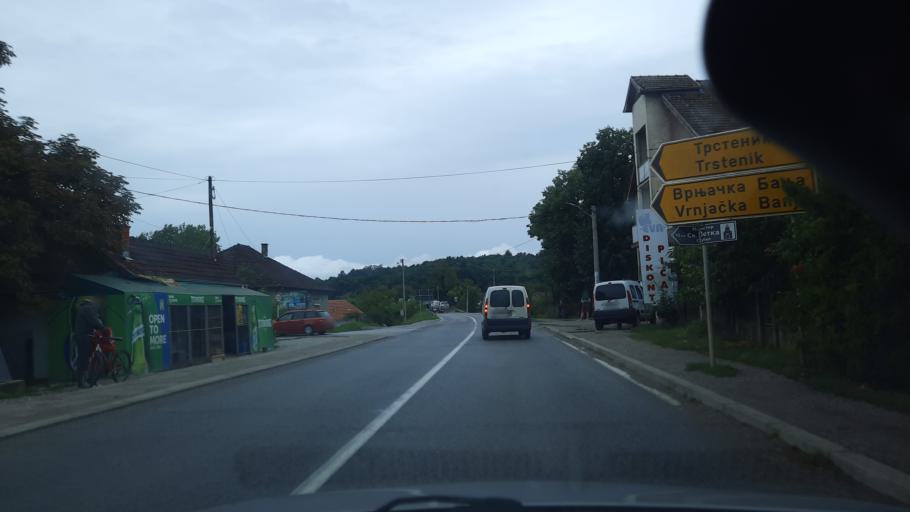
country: RS
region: Central Serbia
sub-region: Raski Okrug
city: Kraljevo
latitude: 43.7257
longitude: 20.7993
